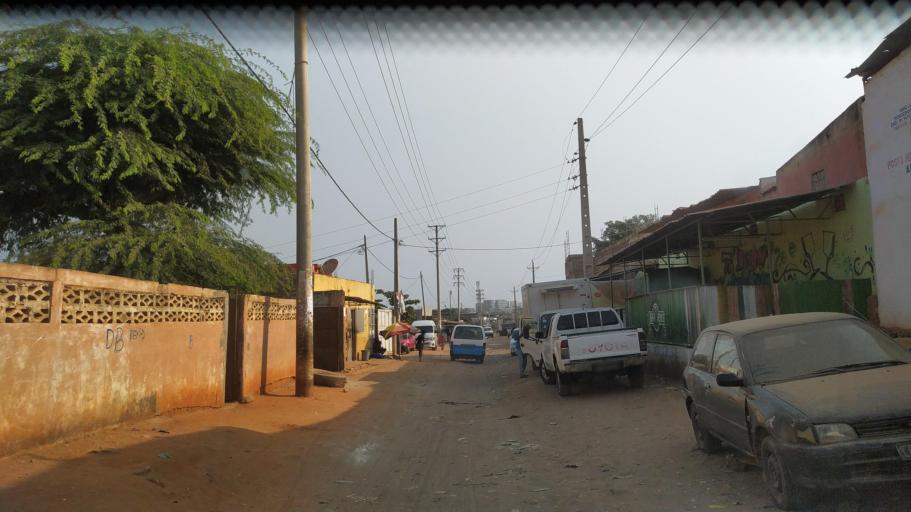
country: AO
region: Luanda
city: Luanda
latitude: -8.8688
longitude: 13.2001
